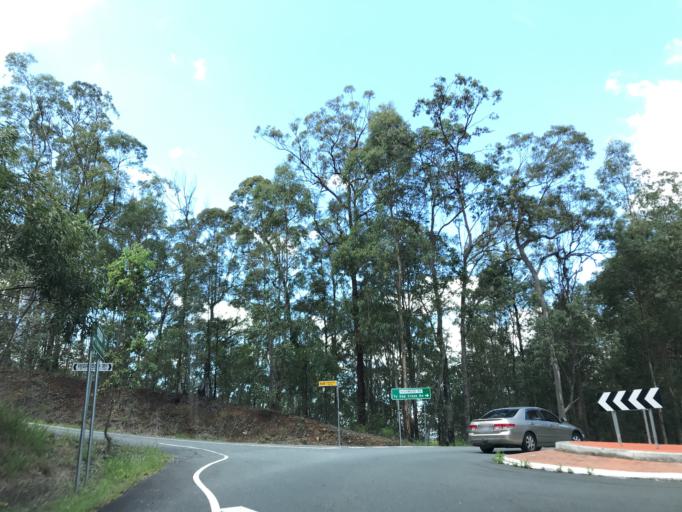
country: AU
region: Queensland
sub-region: Brisbane
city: Kenmore Hills
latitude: -27.4638
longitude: 152.9303
